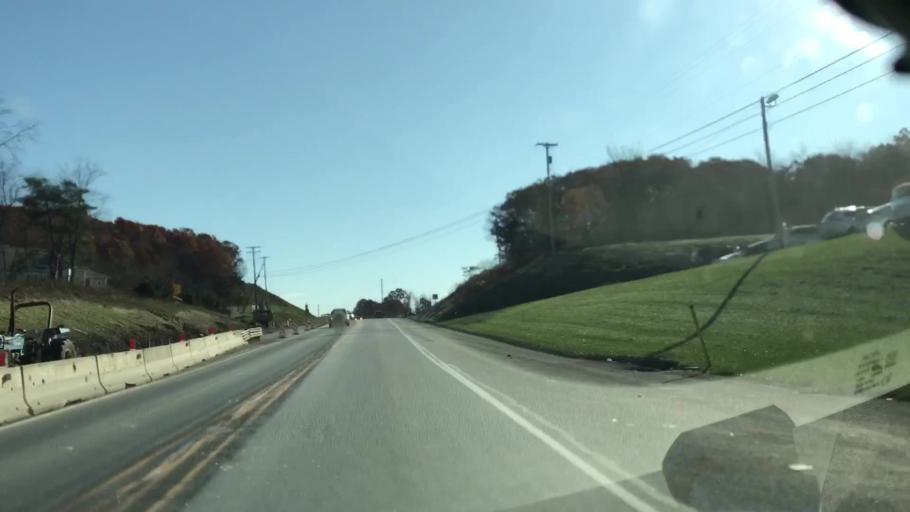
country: US
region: Pennsylvania
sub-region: Butler County
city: Mars
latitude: 40.6910
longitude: -80.0171
